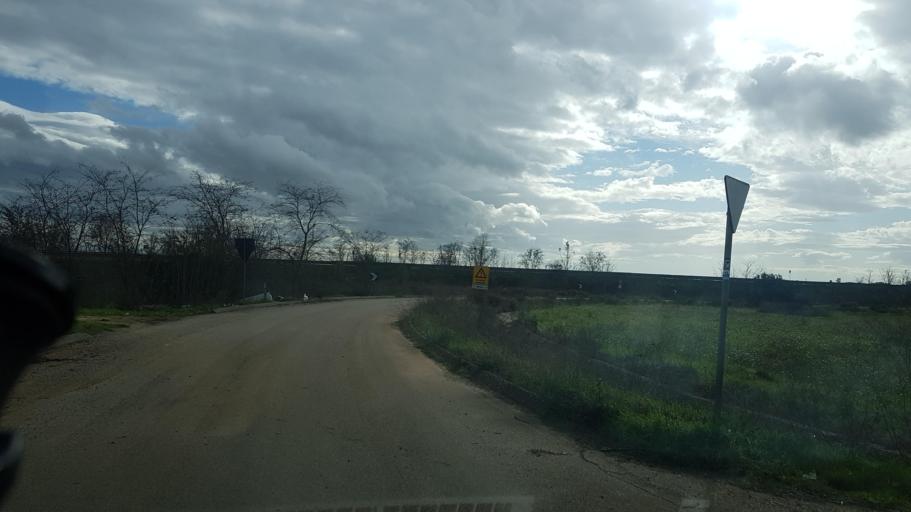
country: IT
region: Apulia
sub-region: Provincia di Brindisi
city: Francavilla Fontana
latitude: 40.5451
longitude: 17.5381
